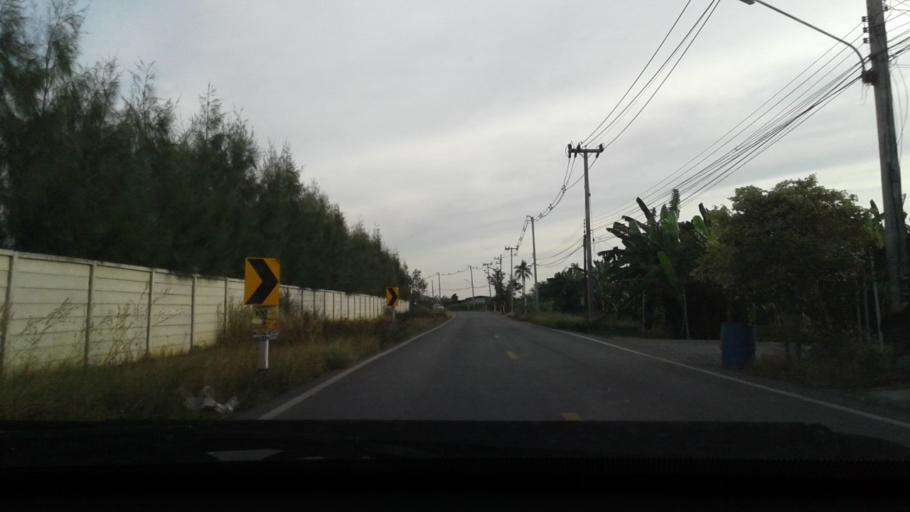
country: TH
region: Nonthaburi
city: Sai Noi
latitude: 13.9136
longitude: 100.2562
